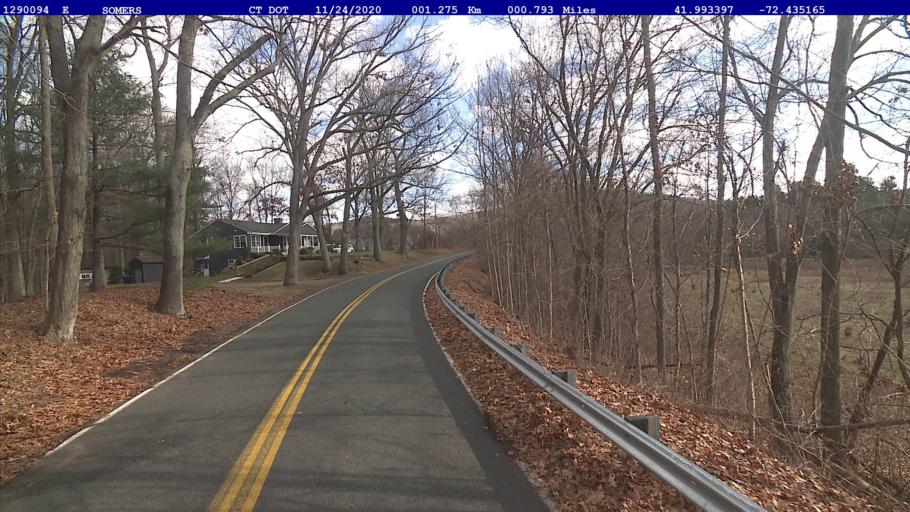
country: US
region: Connecticut
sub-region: Tolland County
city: Somers
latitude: 41.9934
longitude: -72.4352
